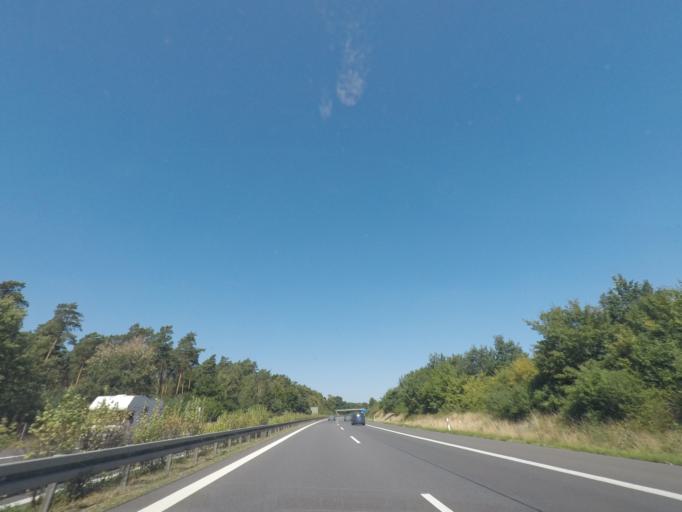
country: DE
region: Brandenburg
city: Bronkow
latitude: 51.6662
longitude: 13.9077
